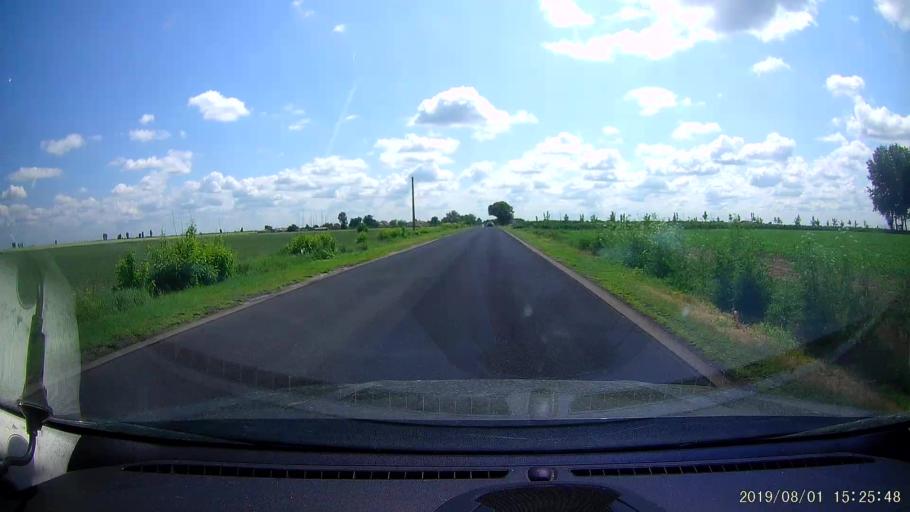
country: RO
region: Braila
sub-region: Comuna Viziru
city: Viziru
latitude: 45.0173
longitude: 27.7298
